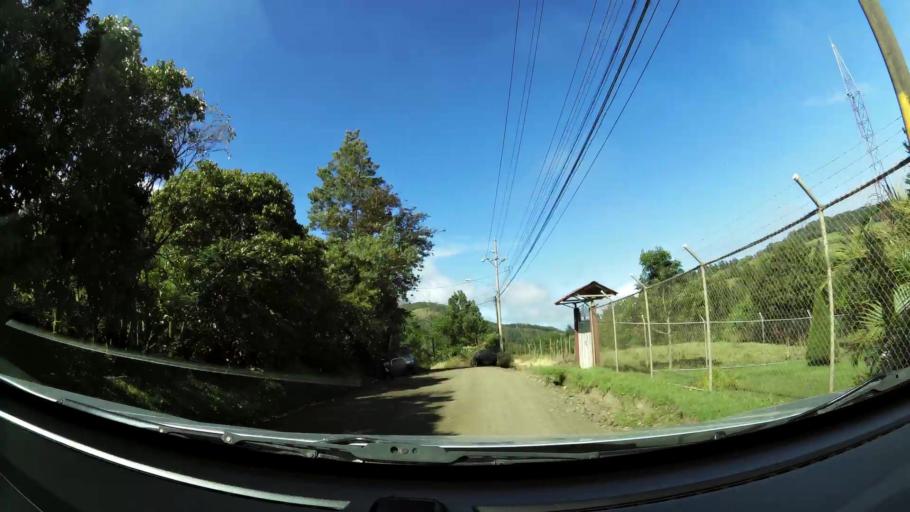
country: CR
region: Guanacaste
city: Juntas
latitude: 10.3293
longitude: -84.8417
